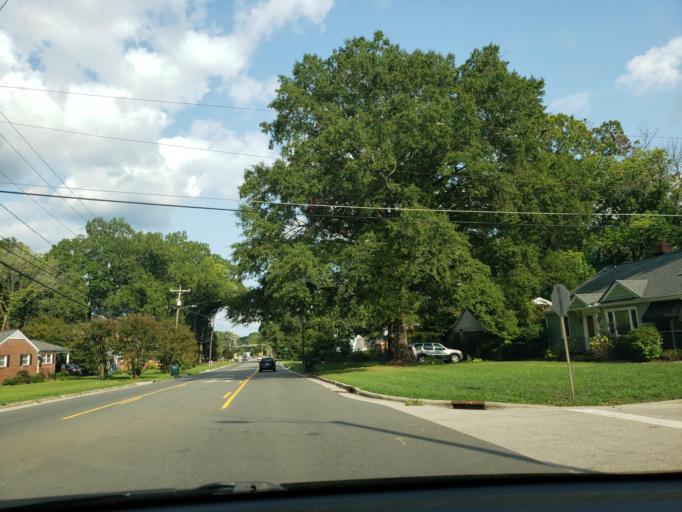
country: US
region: North Carolina
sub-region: Durham County
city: Durham
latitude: 36.0377
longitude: -78.9328
